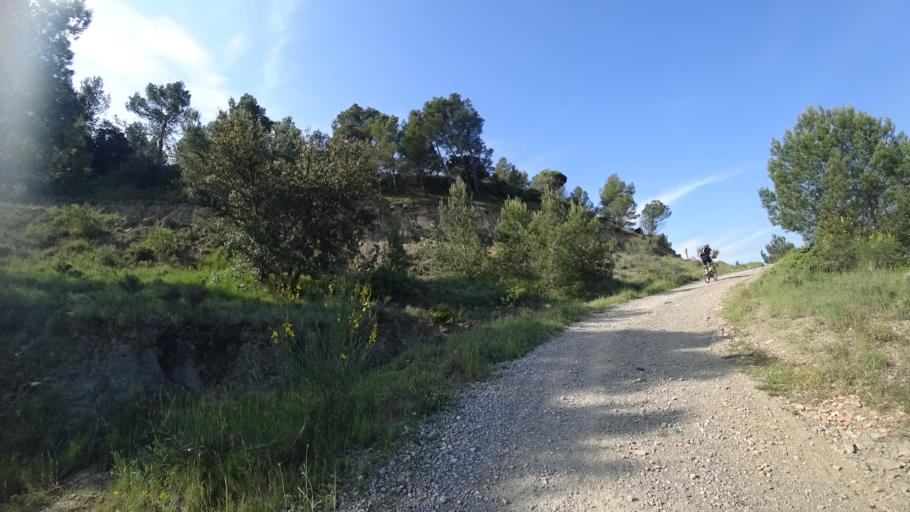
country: FR
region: Languedoc-Roussillon
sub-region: Departement de l'Herault
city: Olonzac
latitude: 43.2484
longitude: 2.7253
